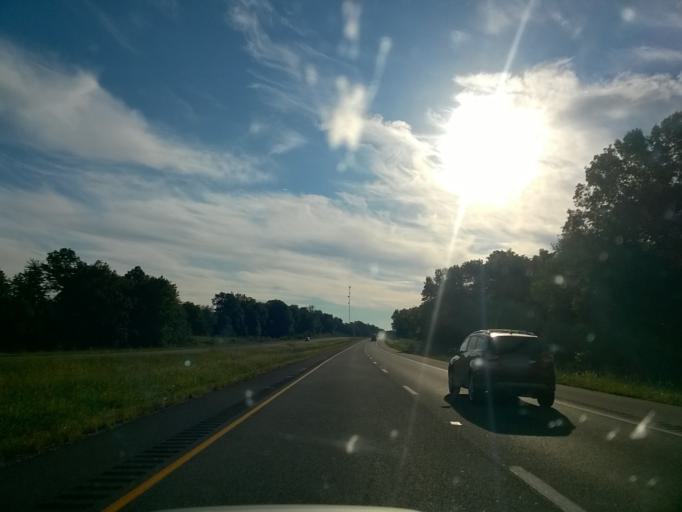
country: US
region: Indiana
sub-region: Warrick County
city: Boonville
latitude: 38.2019
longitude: -87.2074
